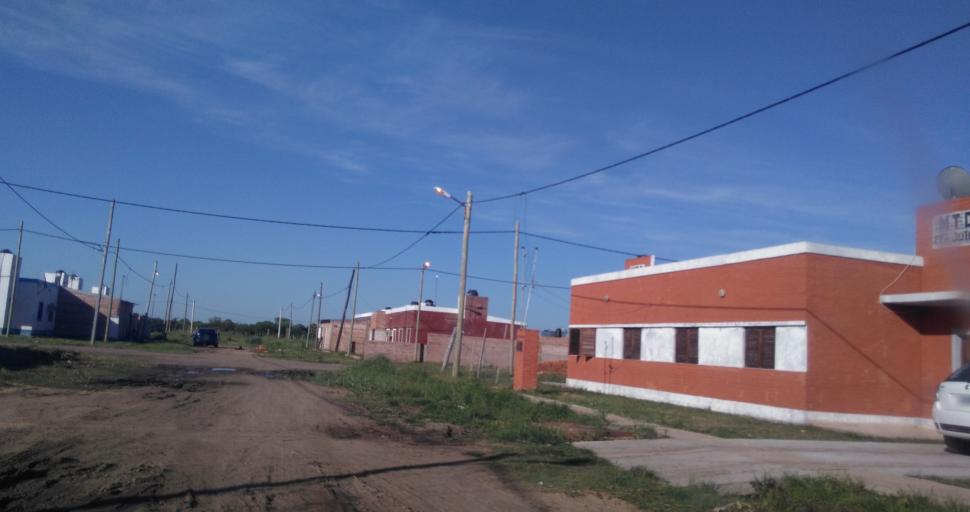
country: AR
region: Chaco
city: Resistencia
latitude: -27.4753
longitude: -59.0267
